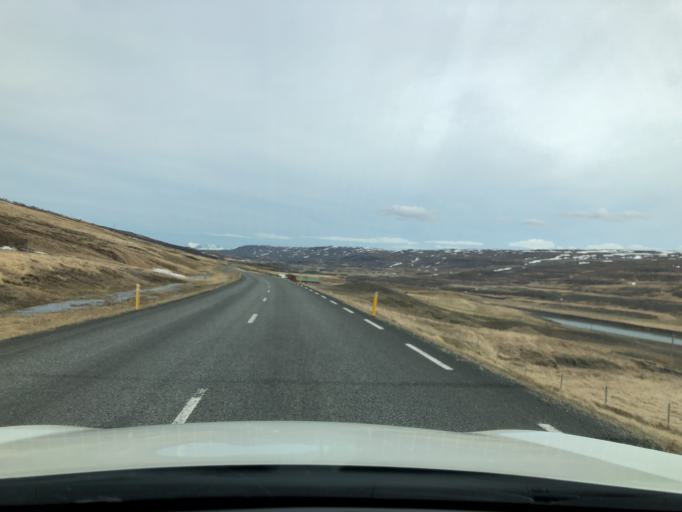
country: IS
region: East
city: Egilsstadir
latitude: 65.3725
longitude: -14.7940
